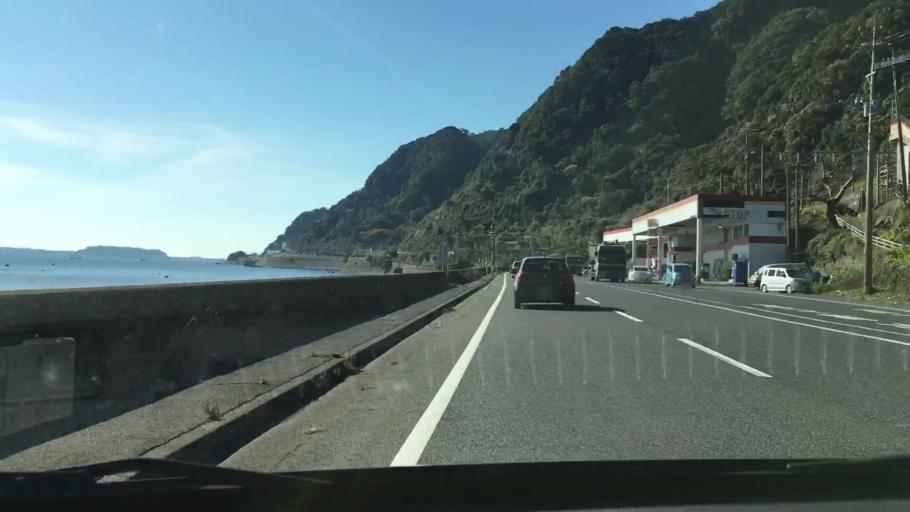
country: JP
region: Kagoshima
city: Kagoshima-shi
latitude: 31.6476
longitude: 130.6047
